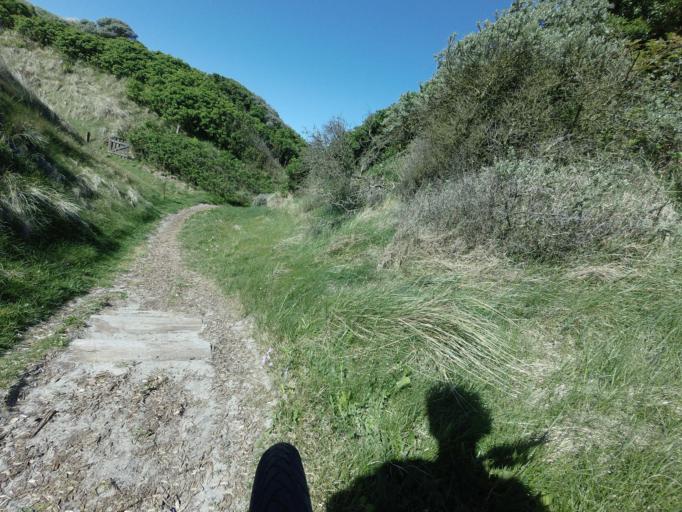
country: DK
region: North Denmark
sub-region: Jammerbugt Kommune
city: Pandrup
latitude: 57.3130
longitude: 9.6537
